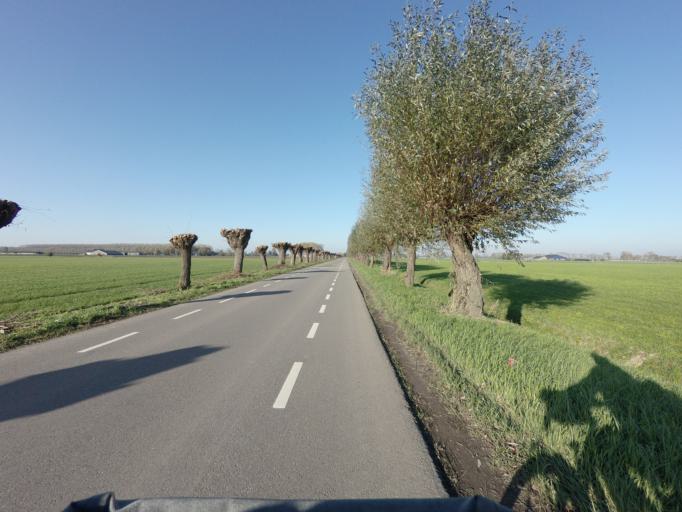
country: NL
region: North Brabant
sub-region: Gemeente Waalwijk
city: Waalwijk
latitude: 51.7540
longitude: 5.0552
